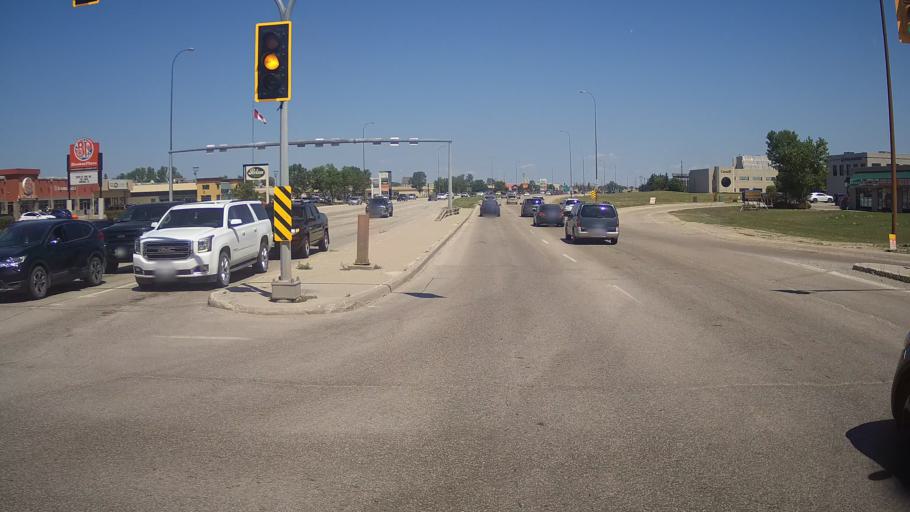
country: CA
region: Manitoba
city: Winnipeg
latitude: 49.8983
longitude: -97.0690
